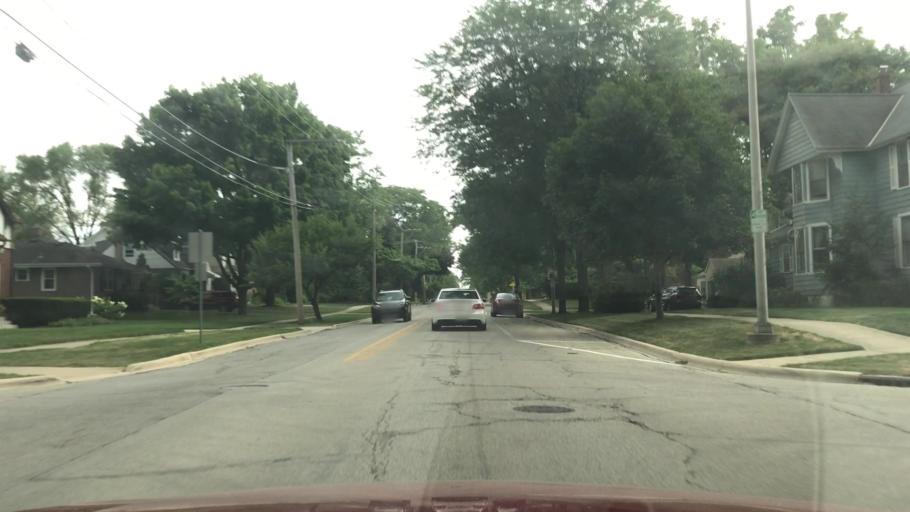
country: US
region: Illinois
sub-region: DuPage County
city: Wheaton
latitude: 41.8657
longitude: -88.0920
